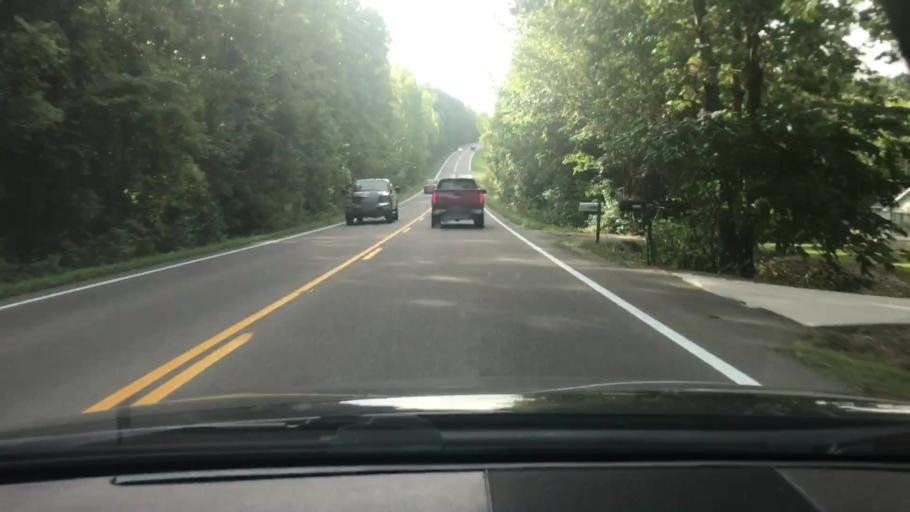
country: US
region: Tennessee
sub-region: Williamson County
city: Fairview
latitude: 36.0161
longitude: -87.1579
